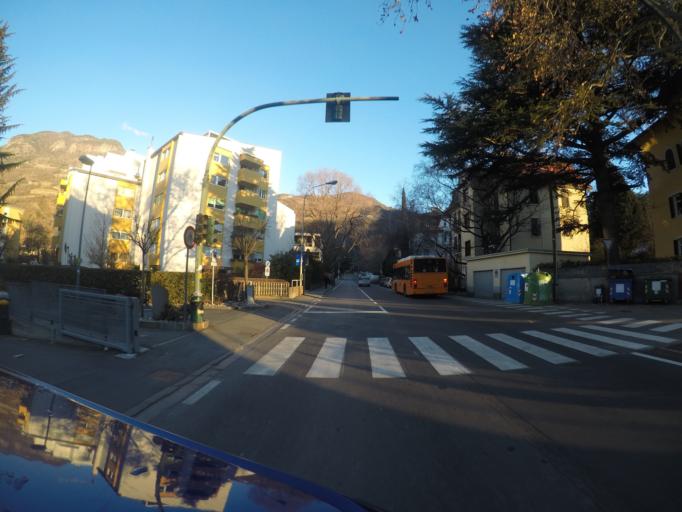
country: IT
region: Trentino-Alto Adige
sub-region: Bolzano
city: Bolzano
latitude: 46.5071
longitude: 11.3472
